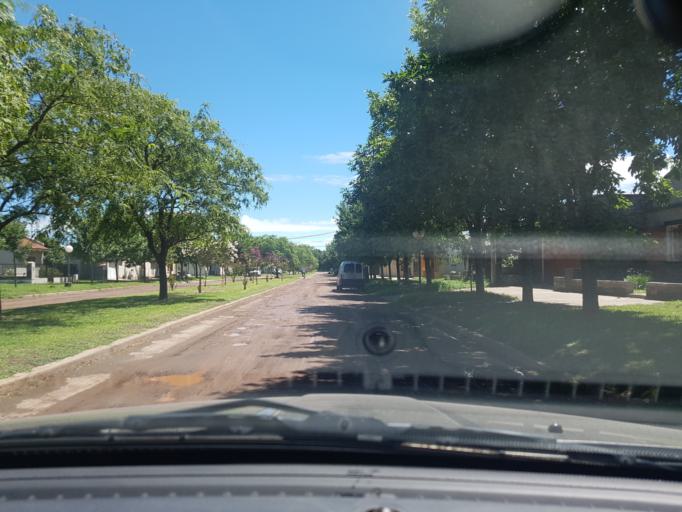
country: AR
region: Cordoba
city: Las Perdices
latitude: -32.7589
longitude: -63.7752
